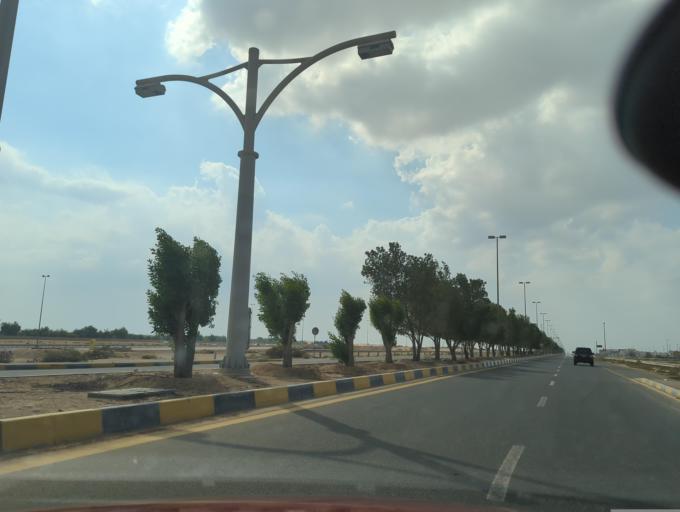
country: AE
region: Abu Dhabi
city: Abu Dhabi
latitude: 24.3679
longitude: 54.7226
